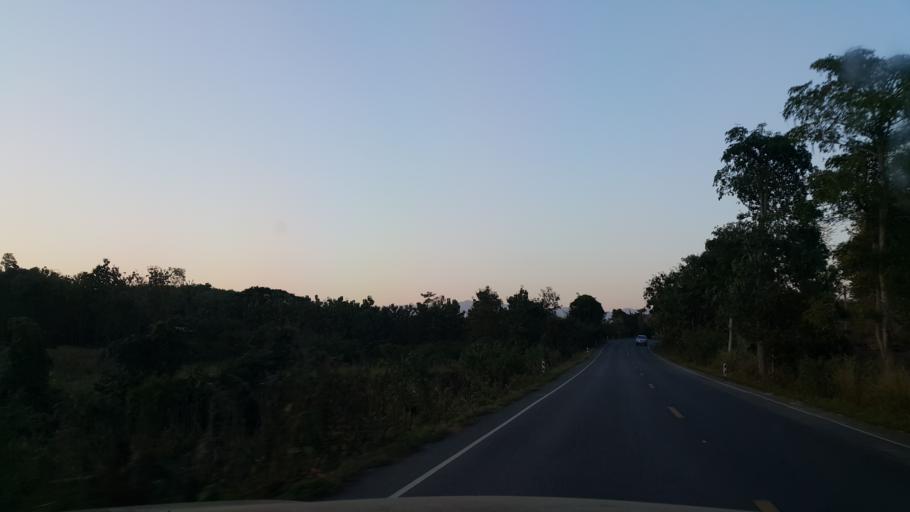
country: TH
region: Phrae
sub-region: Amphoe Wang Chin
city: Wang Chin
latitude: 17.8366
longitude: 99.6415
